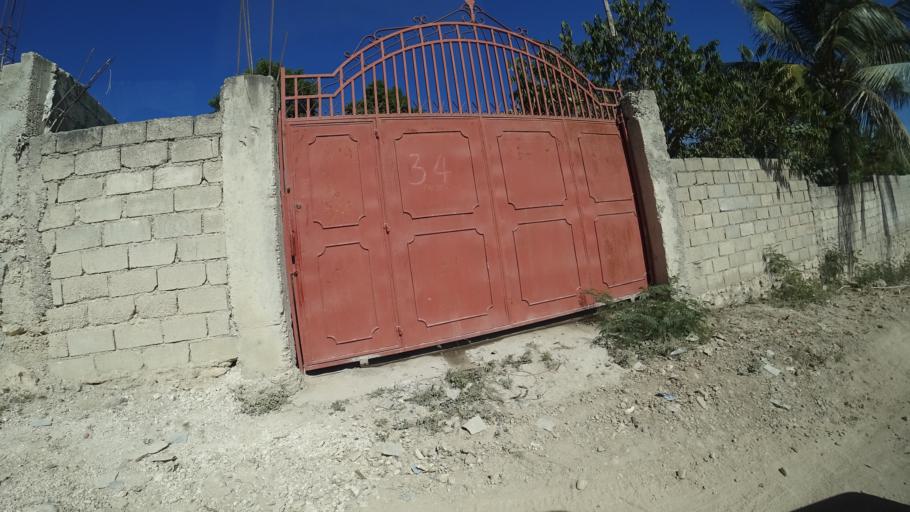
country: HT
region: Ouest
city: Delmas 73
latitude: 18.5574
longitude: -72.2863
